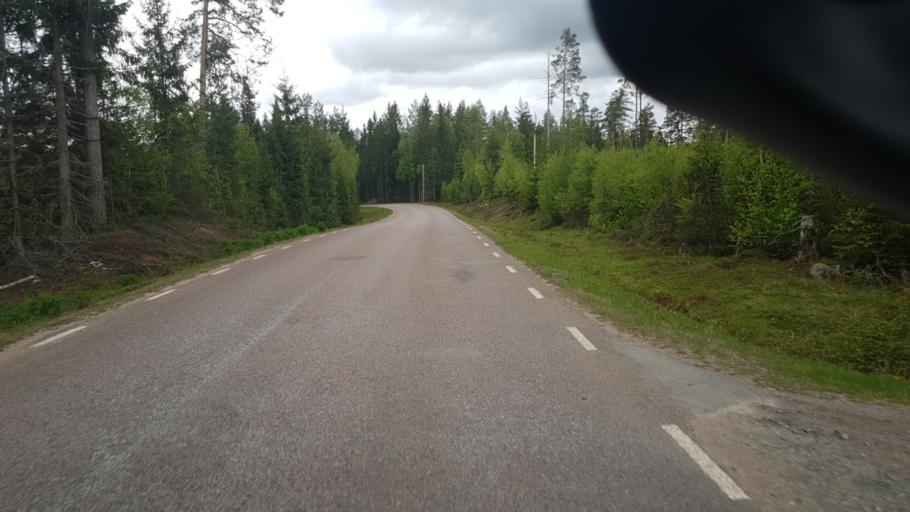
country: SE
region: Vaermland
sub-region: Arvika Kommun
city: Arvika
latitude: 59.8002
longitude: 12.8371
